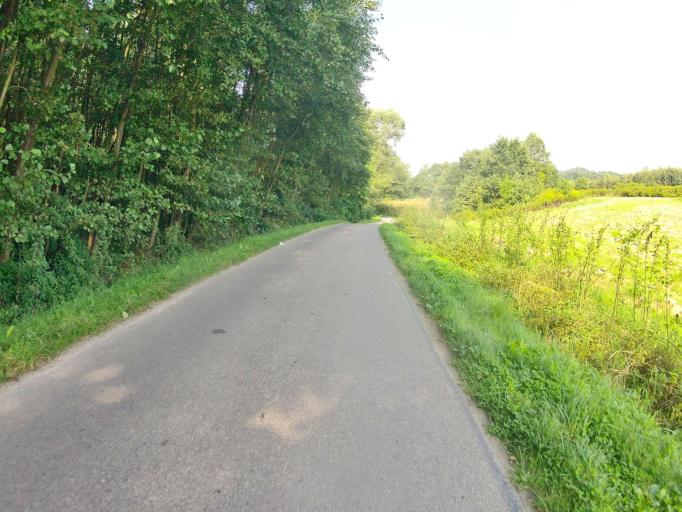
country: PL
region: Subcarpathian Voivodeship
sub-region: Powiat jasielski
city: Brzyska
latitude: 49.7927
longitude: 21.3867
